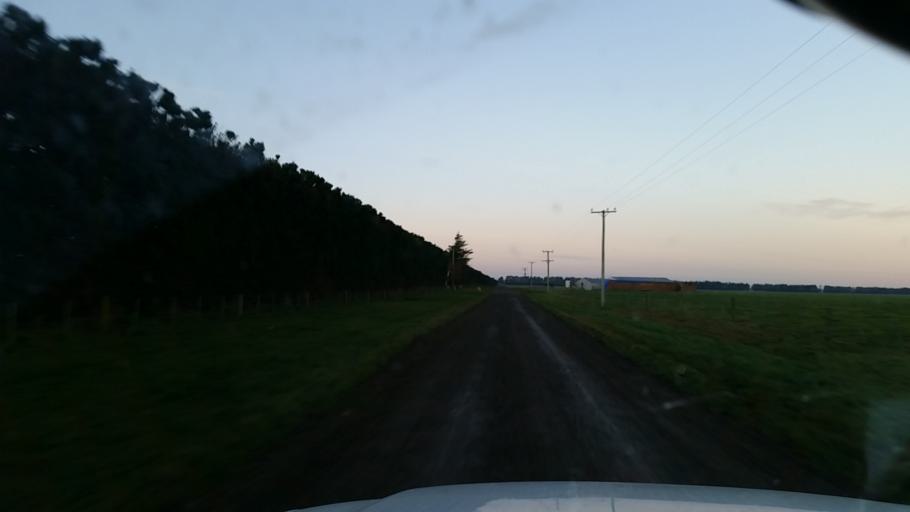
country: NZ
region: Canterbury
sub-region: Ashburton District
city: Tinwald
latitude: -43.9488
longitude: 171.5923
